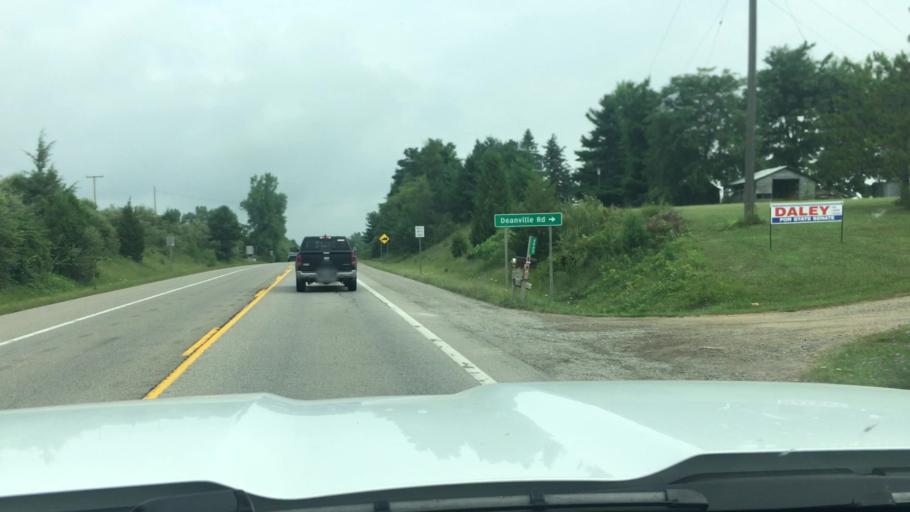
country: US
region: Michigan
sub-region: Sanilac County
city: Brown City
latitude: 43.1794
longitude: -83.0762
